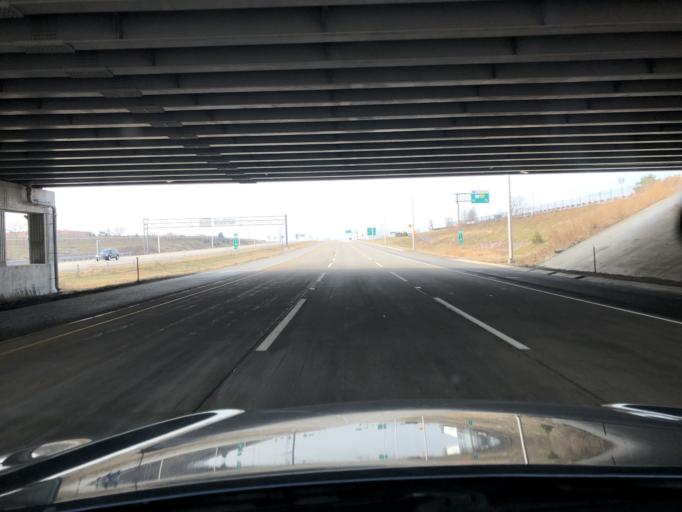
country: US
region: Illinois
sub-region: DuPage County
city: Wood Dale
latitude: 41.9838
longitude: -87.9795
